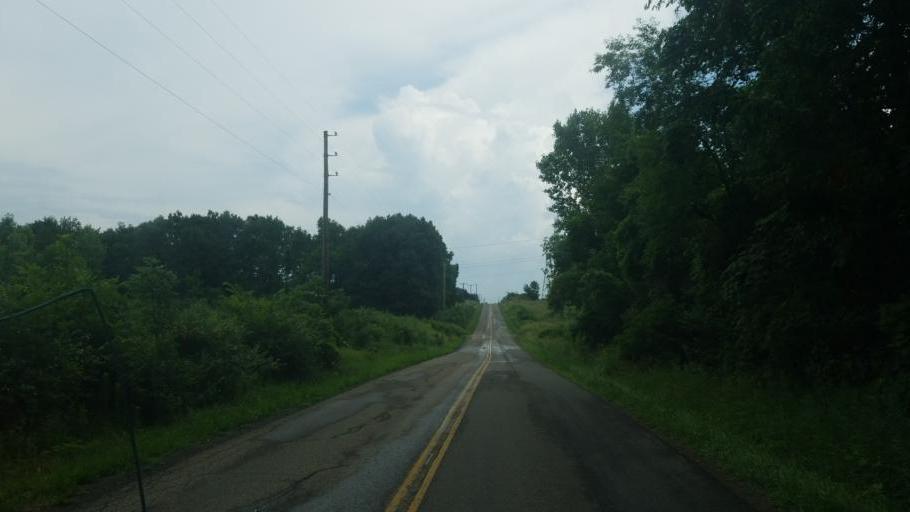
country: US
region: Ohio
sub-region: Summit County
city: Clinton
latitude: 40.8950
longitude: -81.6565
